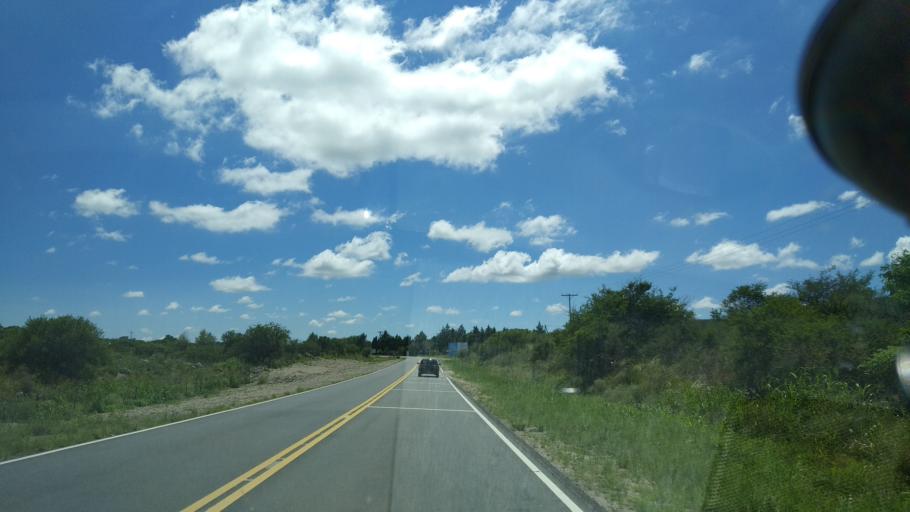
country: AR
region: Cordoba
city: Salsacate
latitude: -31.3485
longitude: -65.0828
